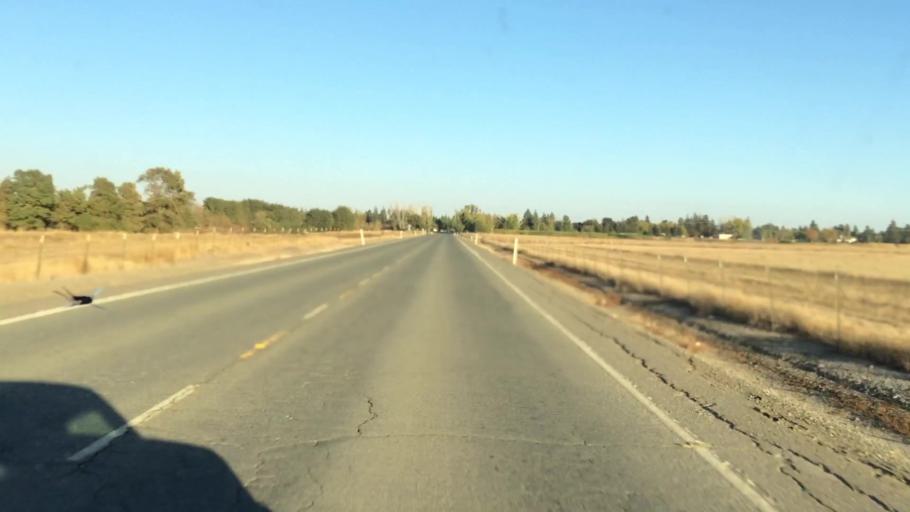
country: US
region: California
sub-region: Sacramento County
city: Laguna
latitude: 38.4377
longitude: -121.4531
